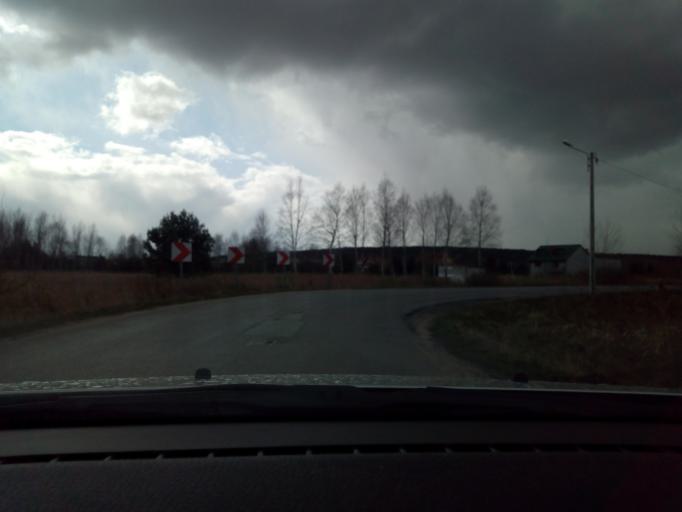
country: PL
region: Swietokrzyskie
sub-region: Powiat skarzyski
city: Skarzysko Koscielne
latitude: 51.1441
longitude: 20.8862
